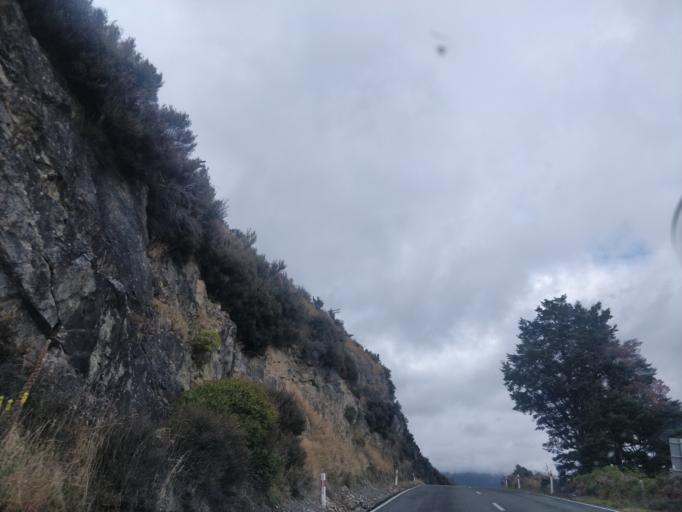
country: NZ
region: Canterbury
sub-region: Waimakariri District
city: Oxford
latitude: -43.0081
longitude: 171.7293
